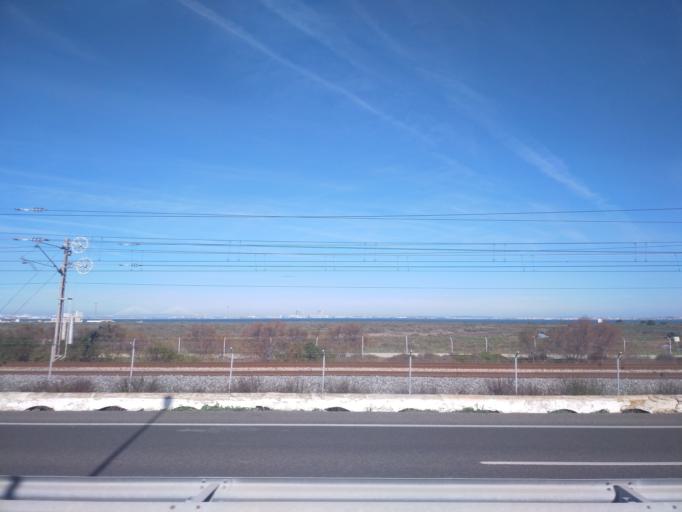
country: ES
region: Andalusia
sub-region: Provincia de Cadiz
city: San Fernando
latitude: 36.4598
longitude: -6.2442
